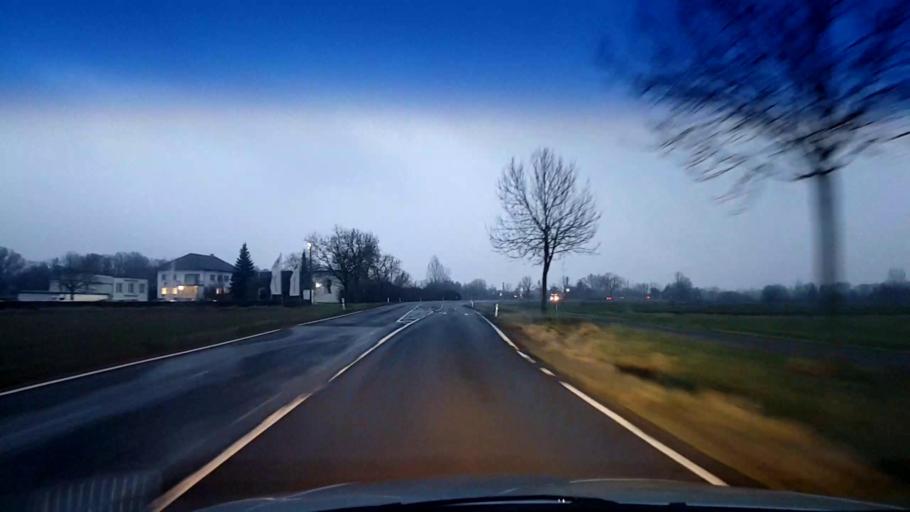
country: DE
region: Bavaria
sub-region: Upper Franconia
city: Breitengussbach
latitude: 49.9891
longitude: 10.8838
